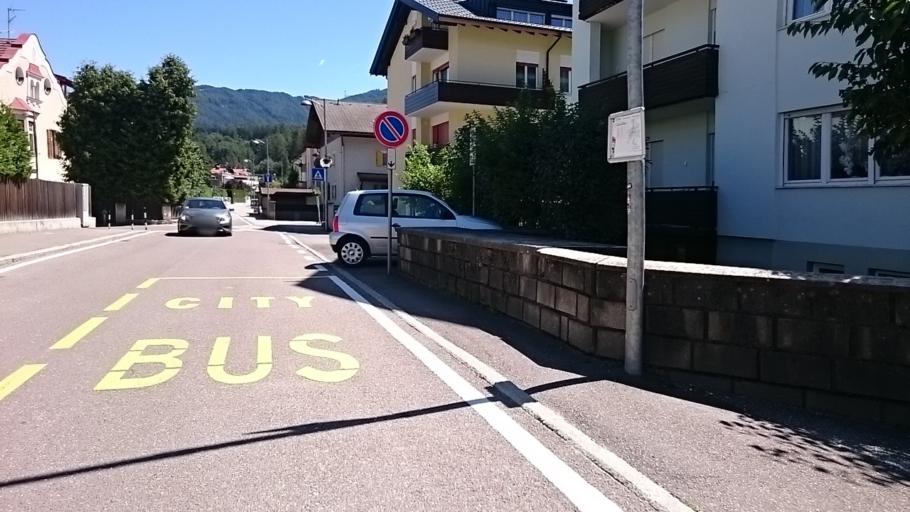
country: IT
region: Trentino-Alto Adige
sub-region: Bolzano
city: Brunico
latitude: 46.7927
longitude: 11.9442
